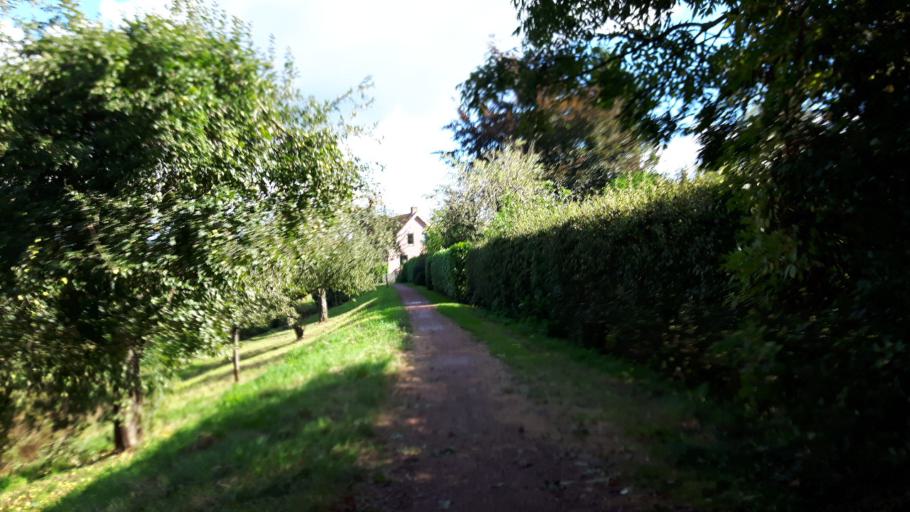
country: NL
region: South Holland
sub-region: Gemeente Leerdam
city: Leerdam
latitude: 51.8733
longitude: 5.0709
